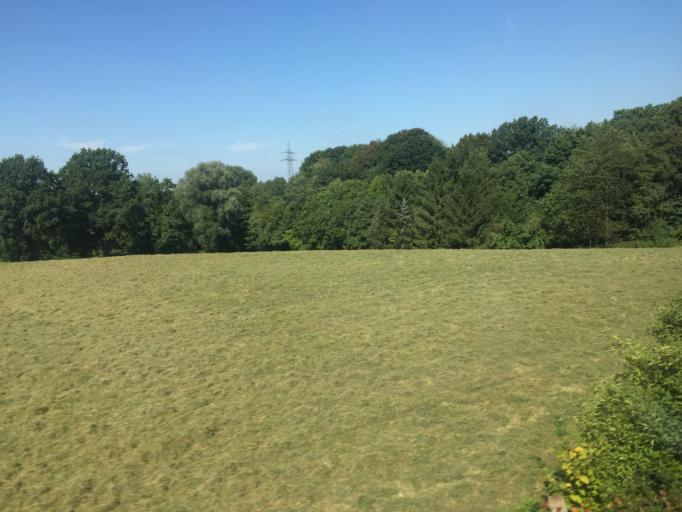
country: DE
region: Schleswig-Holstein
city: Tremsbuttel
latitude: 53.7638
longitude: 10.3292
